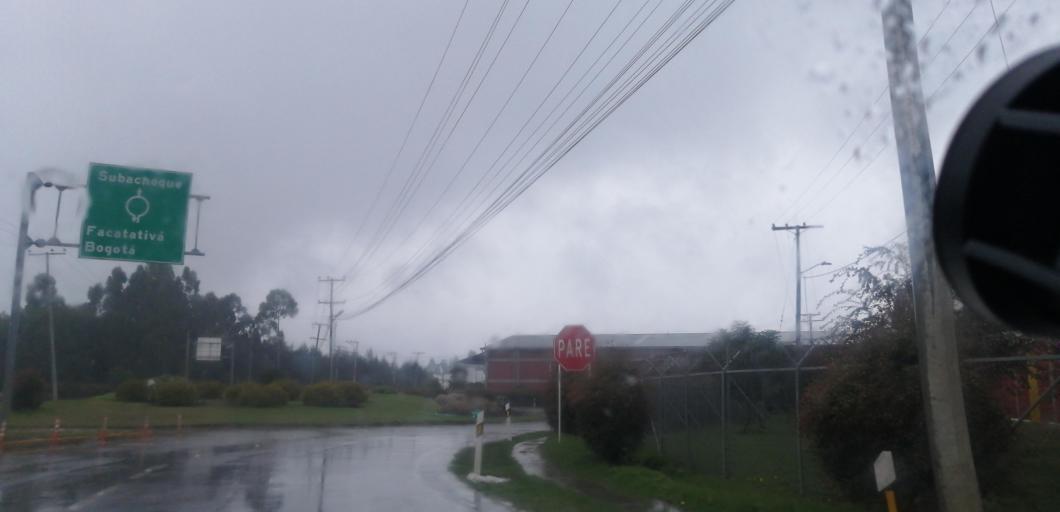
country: CO
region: Cundinamarca
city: Madrid
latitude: 4.7421
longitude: -74.2575
